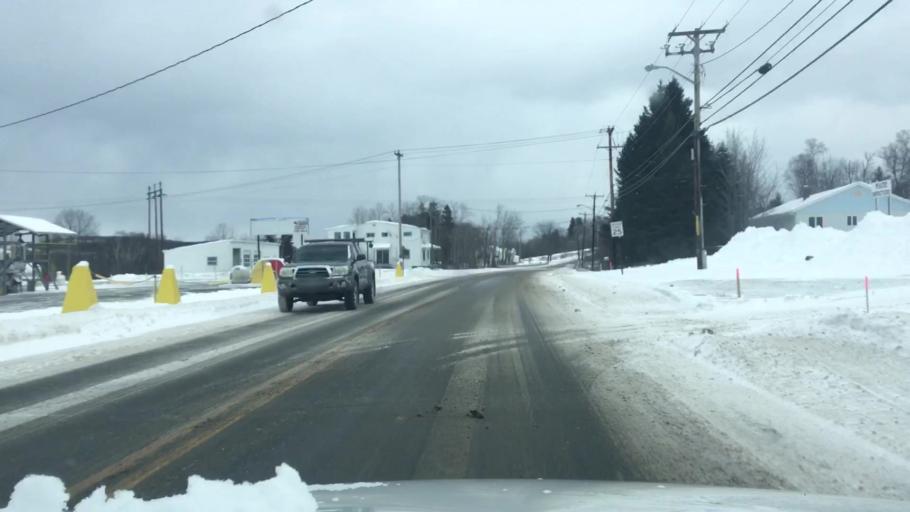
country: US
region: Maine
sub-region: Aroostook County
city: Madawaska
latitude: 47.3528
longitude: -68.3000
